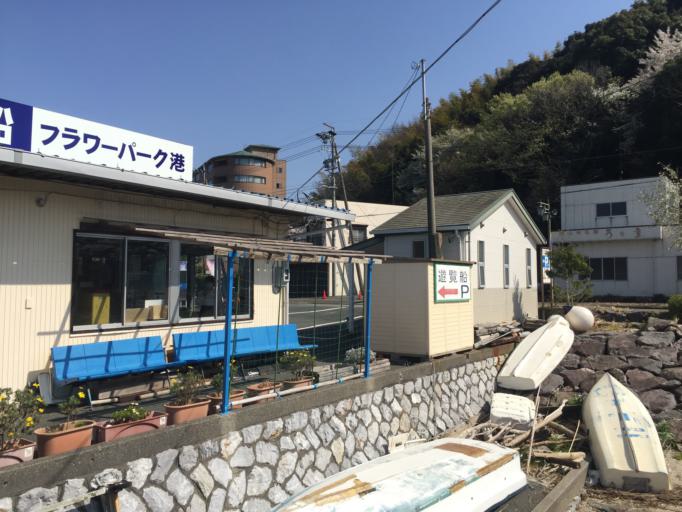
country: JP
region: Shizuoka
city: Kosai-shi
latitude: 34.7648
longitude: 137.6266
